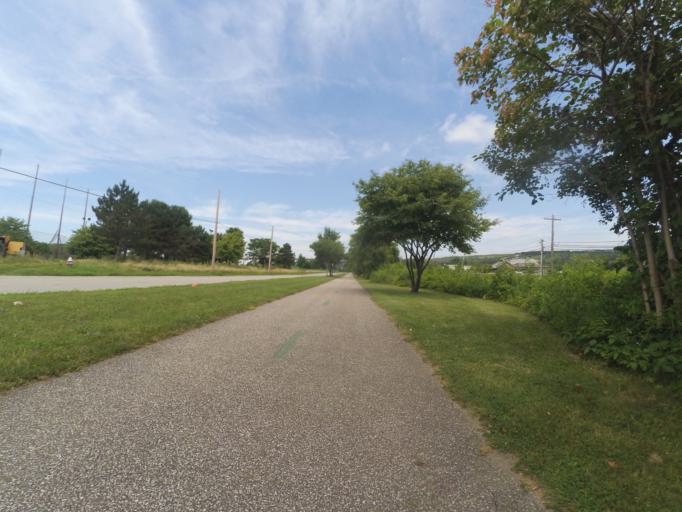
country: US
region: Ohio
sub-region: Cuyahoga County
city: Valley View
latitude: 41.3982
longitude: -81.6273
